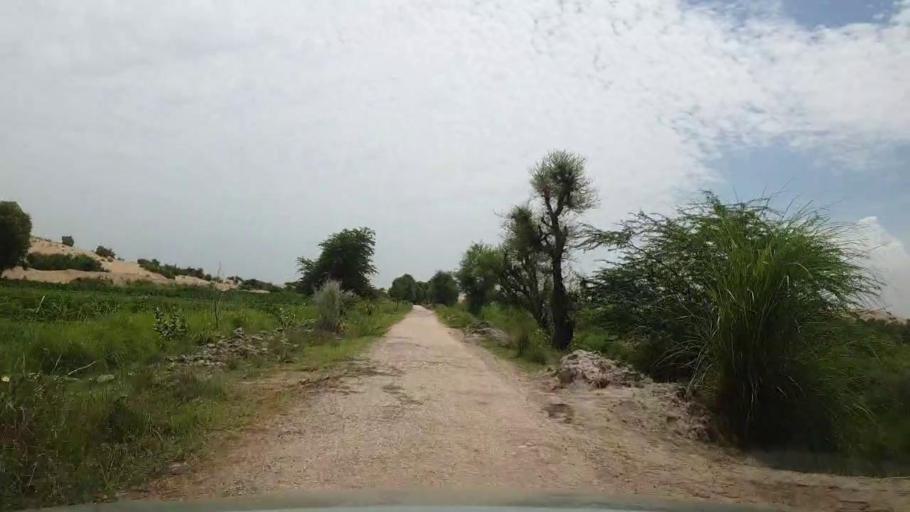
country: PK
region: Sindh
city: Bozdar
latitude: 27.0670
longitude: 68.9666
